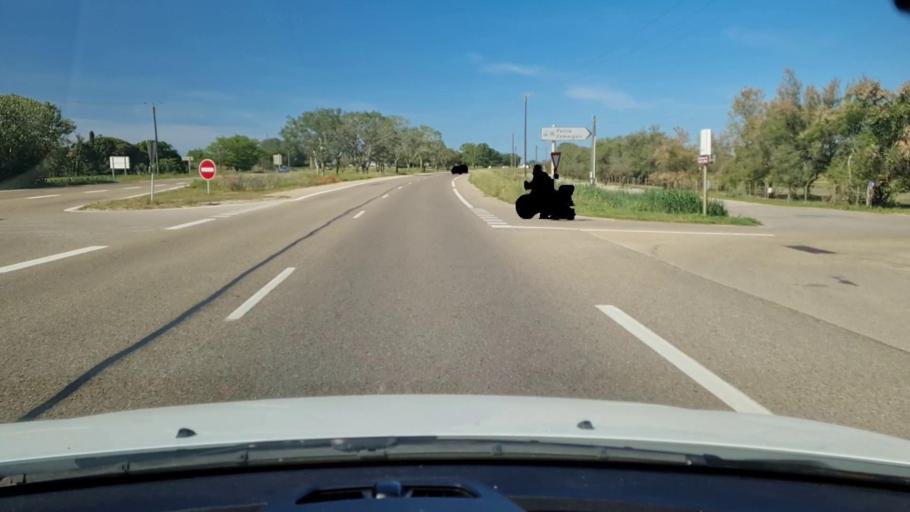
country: FR
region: Languedoc-Roussillon
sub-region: Departement du Gard
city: Aigues-Mortes
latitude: 43.5626
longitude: 4.1590
